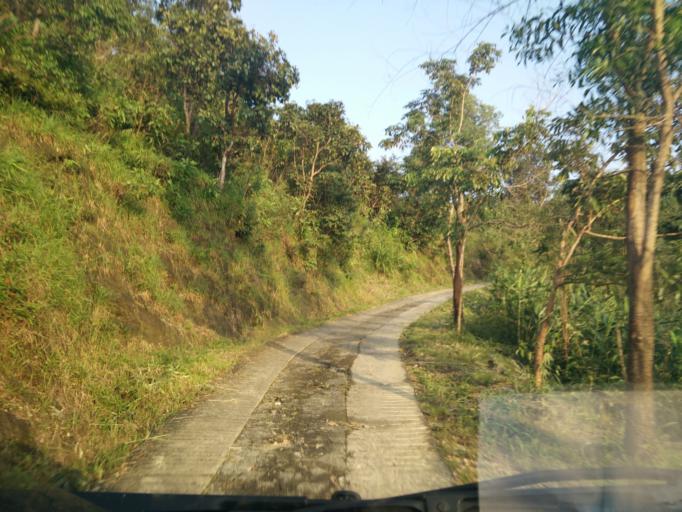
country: MM
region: Mon
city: Thaton
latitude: 16.9296
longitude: 97.3819
